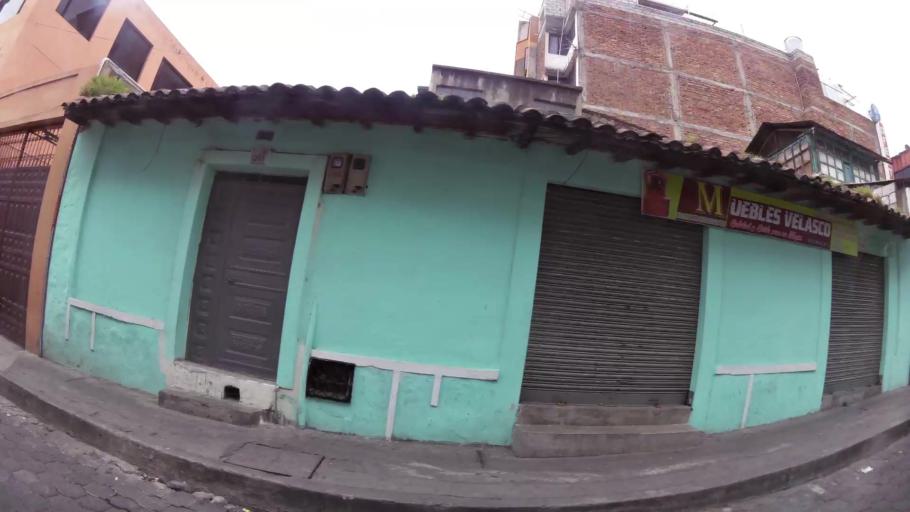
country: EC
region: Cotopaxi
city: Latacunga
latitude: -0.9329
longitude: -78.6185
